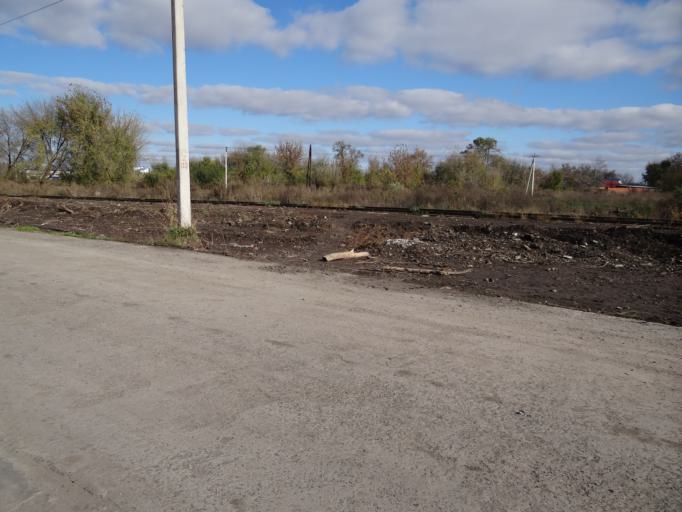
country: RU
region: Kursk
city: Kursk
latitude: 51.6560
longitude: 36.1544
